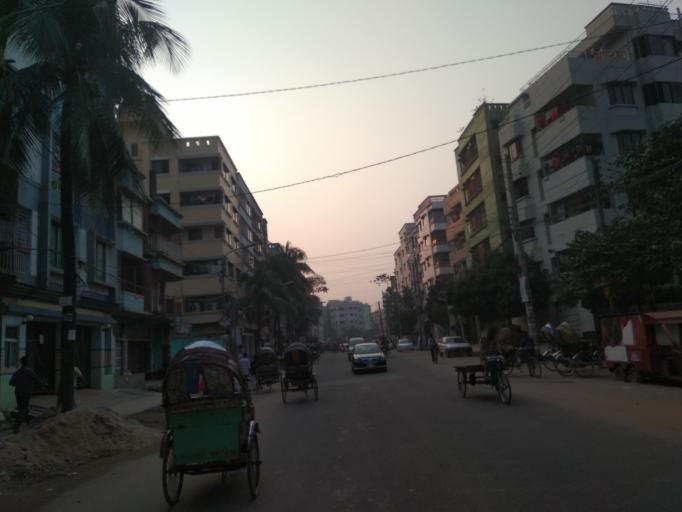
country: BD
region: Dhaka
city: Azimpur
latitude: 23.8102
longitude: 90.3658
